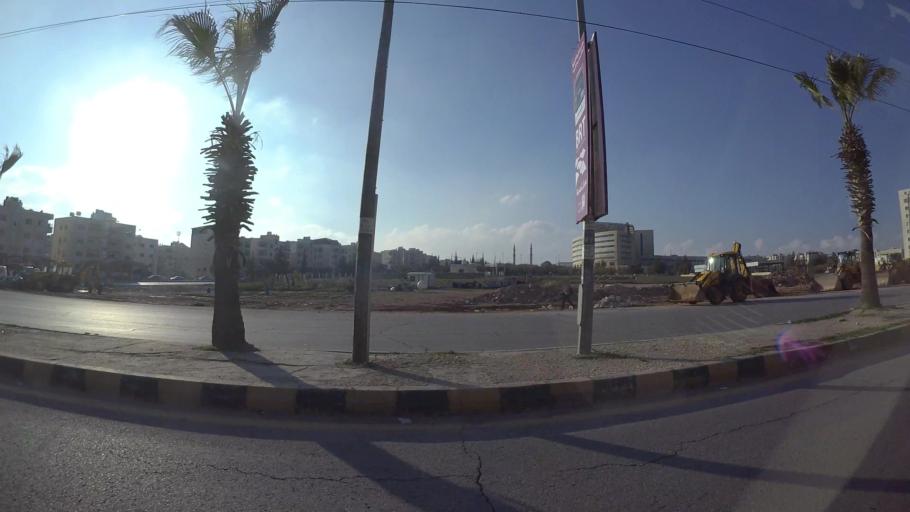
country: JO
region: Amman
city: Amman
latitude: 31.9808
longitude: 35.9406
